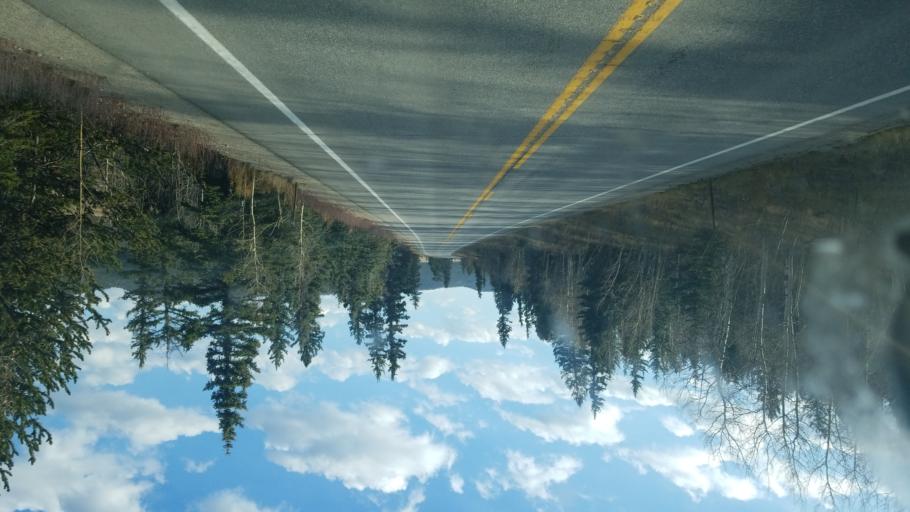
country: US
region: Colorado
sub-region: Chaffee County
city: Buena Vista
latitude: 38.9002
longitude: -105.9900
